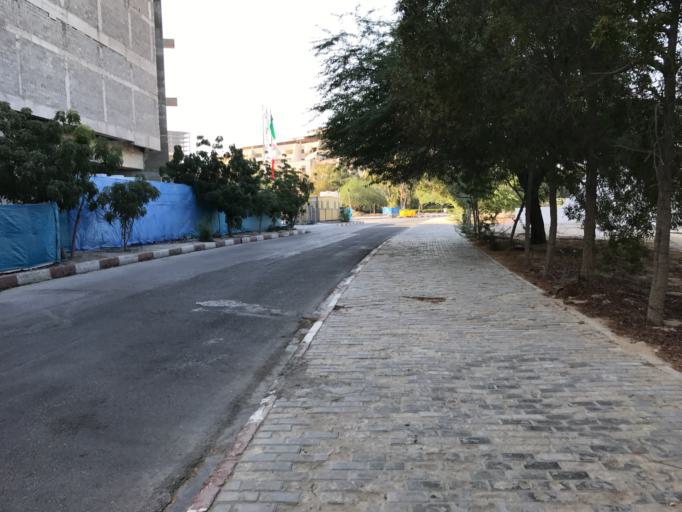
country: IR
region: Hormozgan
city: Kish
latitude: 26.5383
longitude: 54.0247
